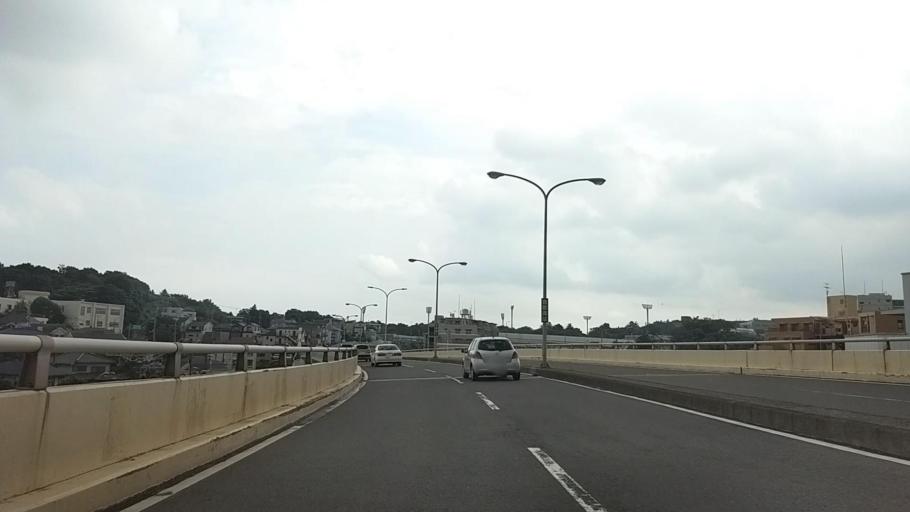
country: JP
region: Kanagawa
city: Yokohama
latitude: 35.4768
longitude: 139.6018
